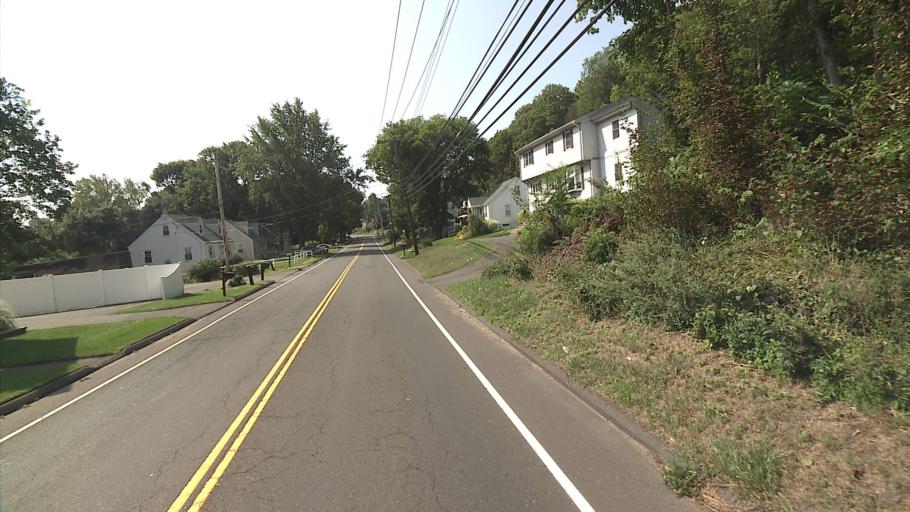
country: US
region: Connecticut
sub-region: New Haven County
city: East Haven
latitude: 41.2881
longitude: -72.8689
